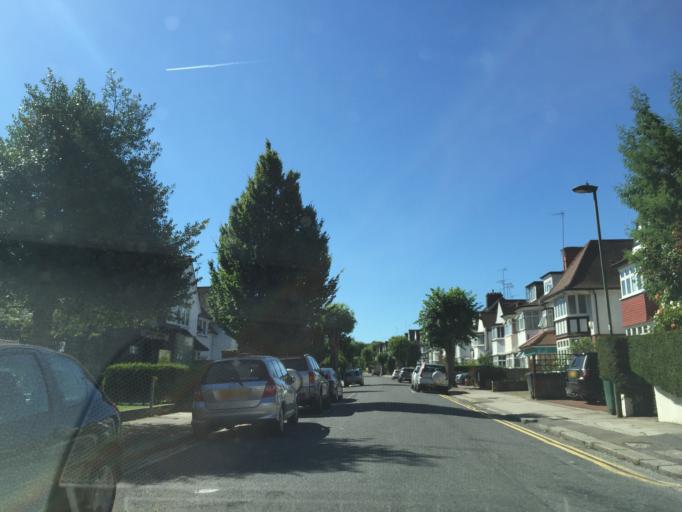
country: GB
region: England
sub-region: Greater London
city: Belsize Park
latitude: 51.5709
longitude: -0.1933
